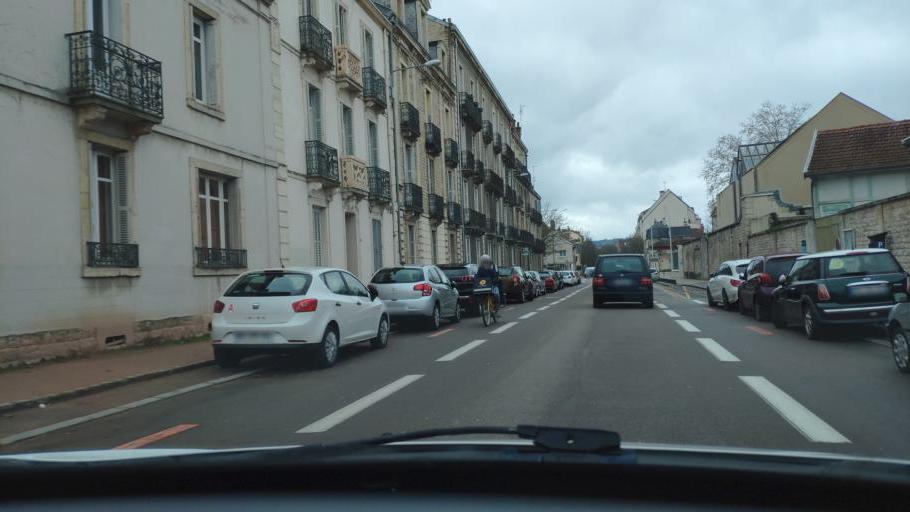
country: FR
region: Bourgogne
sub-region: Departement de la Cote-d'Or
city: Dijon
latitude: 47.3168
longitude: 5.0393
